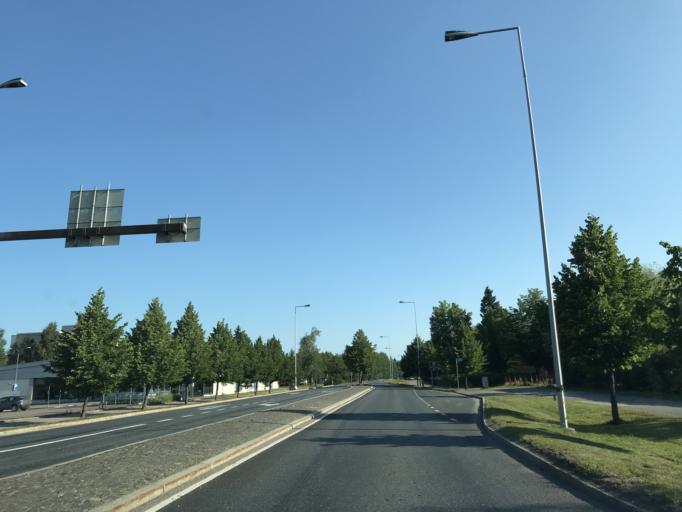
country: FI
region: Paijanne Tavastia
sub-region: Lahti
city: Orimattila
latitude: 60.8057
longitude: 25.7288
